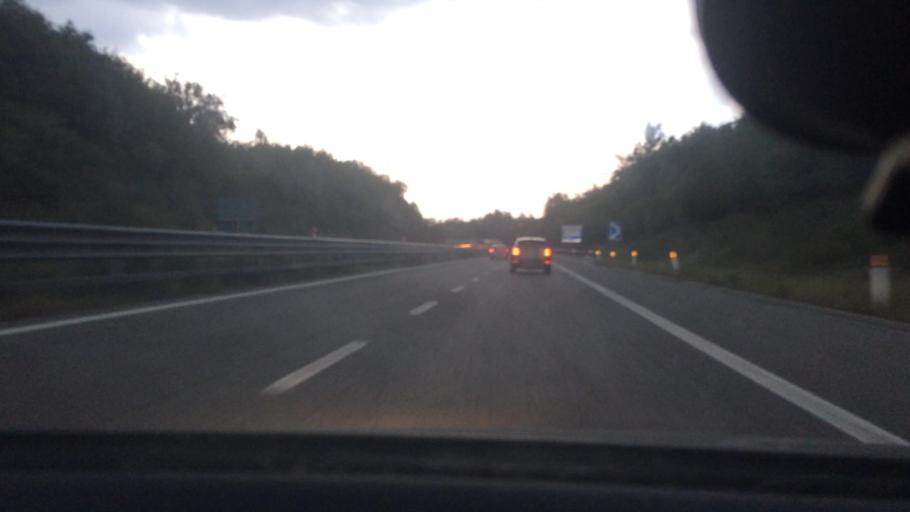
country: IT
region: Lombardy
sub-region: Citta metropolitana di Milano
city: Vanzaghello
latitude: 45.5690
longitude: 8.7751
